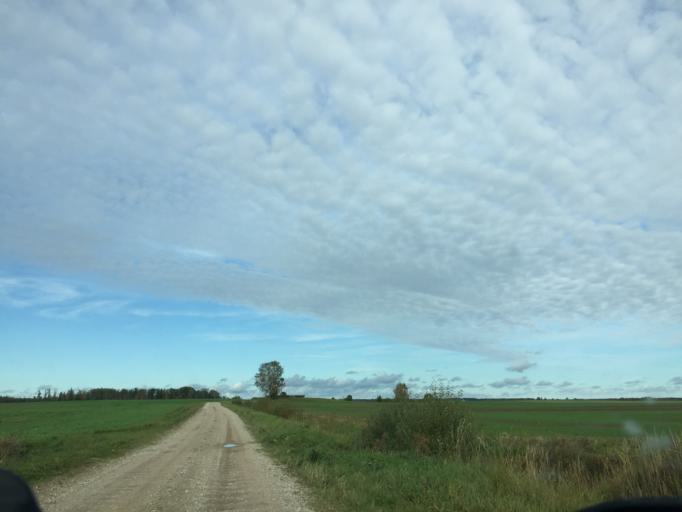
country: LV
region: Jaunpils
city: Jaunpils
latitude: 56.6499
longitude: 23.0782
